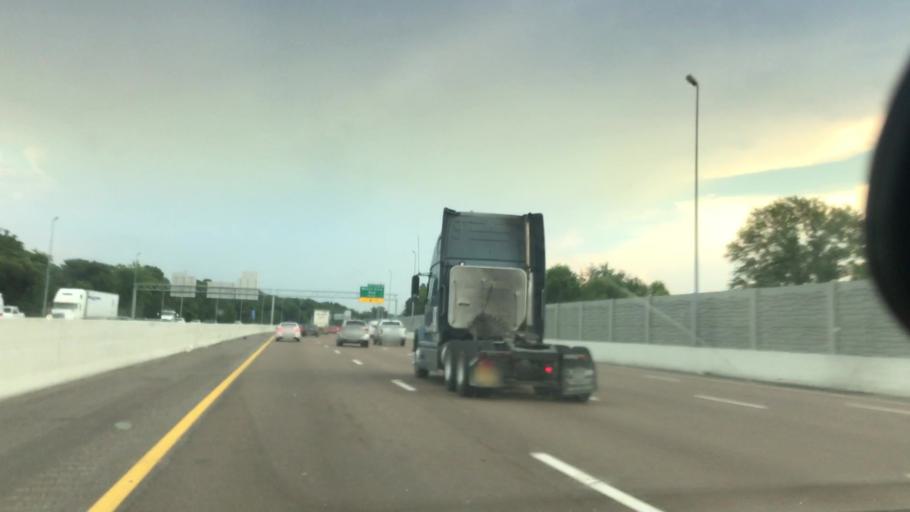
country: US
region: Tennessee
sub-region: Shelby County
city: Bartlett
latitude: 35.1459
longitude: -89.8767
